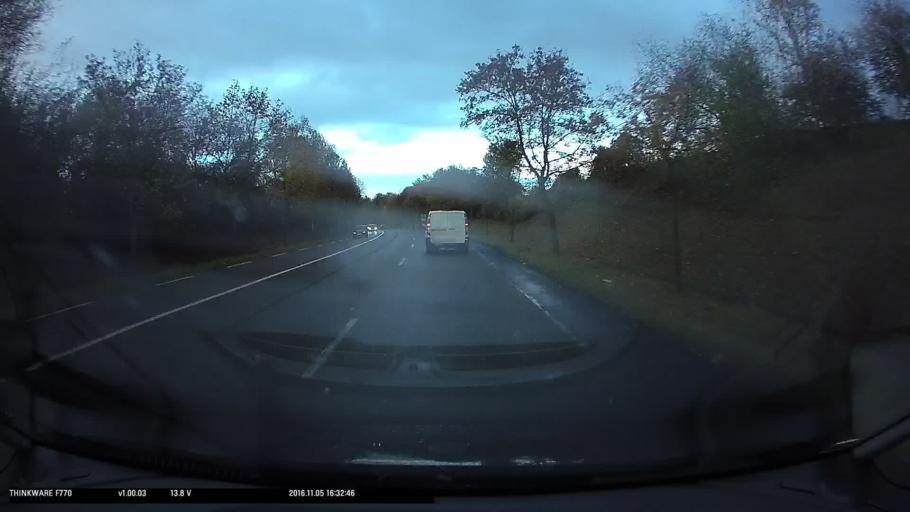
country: FR
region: Ile-de-France
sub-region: Departement du Val-d'Oise
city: Sagy
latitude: 49.0569
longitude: 1.9625
